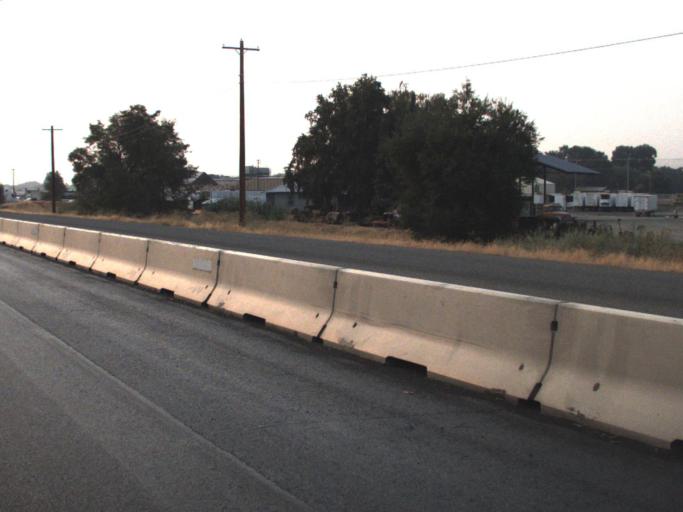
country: US
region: Washington
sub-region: Yakima County
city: Toppenish
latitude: 46.3777
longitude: -120.3350
